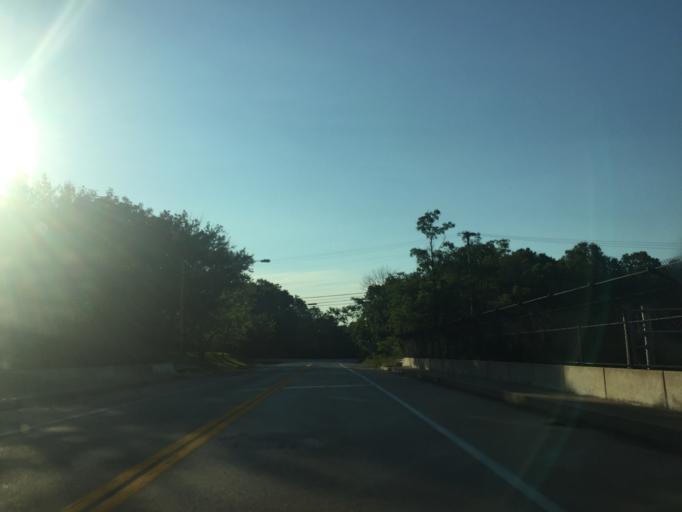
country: US
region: Maryland
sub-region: Baltimore County
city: Arbutus
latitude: 39.2418
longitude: -76.7139
